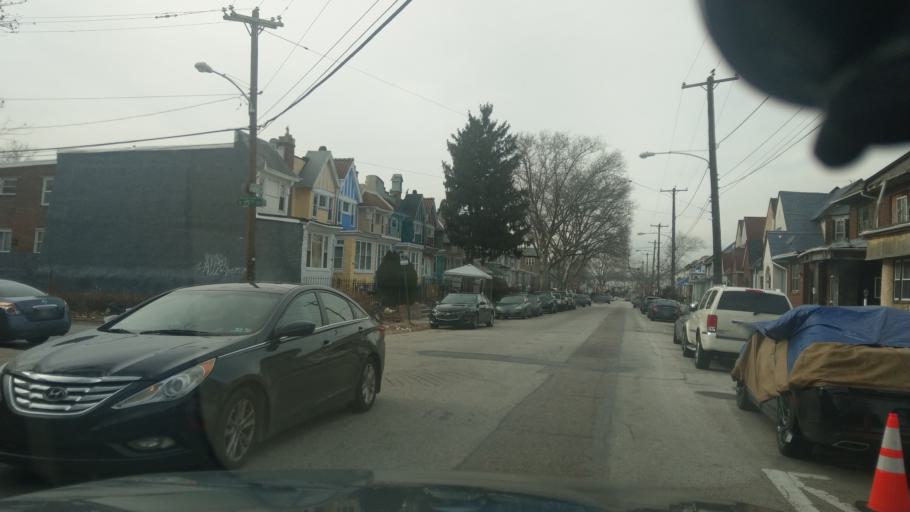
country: US
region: Pennsylvania
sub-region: Montgomery County
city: Wyncote
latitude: 40.0432
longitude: -75.1456
